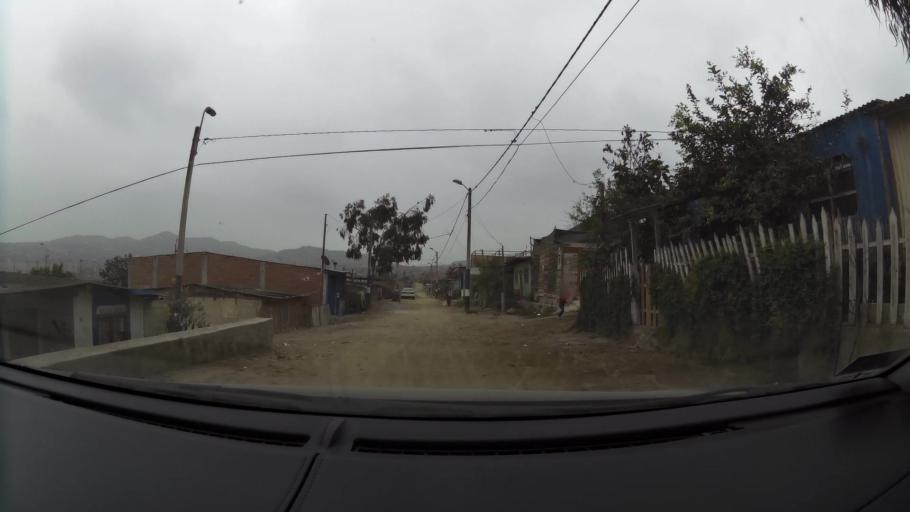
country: PE
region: Lima
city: Ventanilla
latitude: -11.8467
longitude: -77.1424
